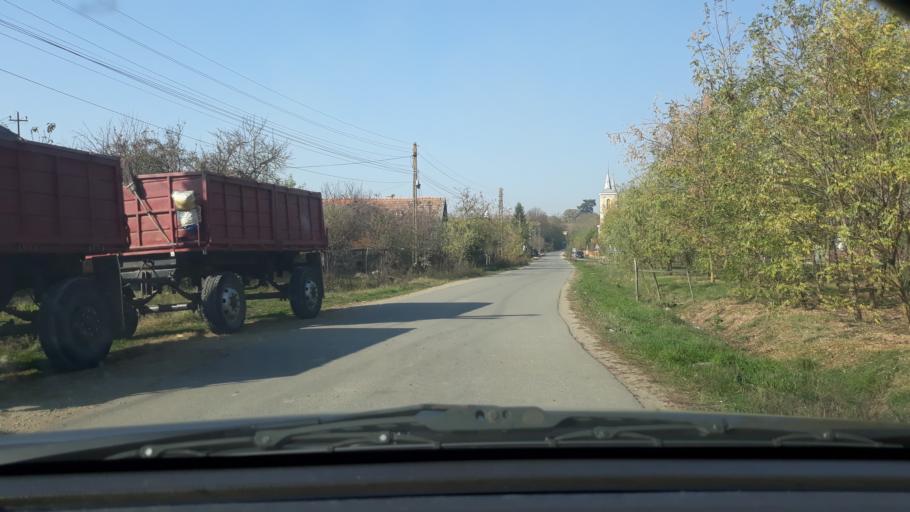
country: RO
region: Bihor
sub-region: Comuna Tarcea
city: Galospetreu
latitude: 47.4796
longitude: 22.2193
